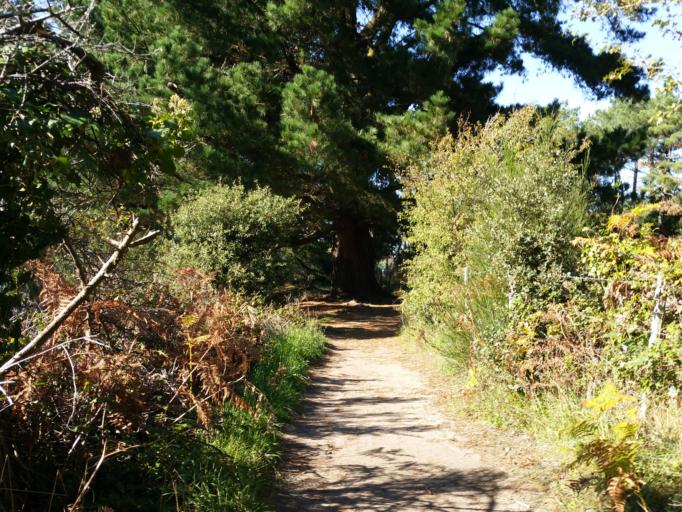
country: FR
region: Brittany
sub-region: Departement du Morbihan
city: Locmariaquer
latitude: 47.5889
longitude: -2.9263
